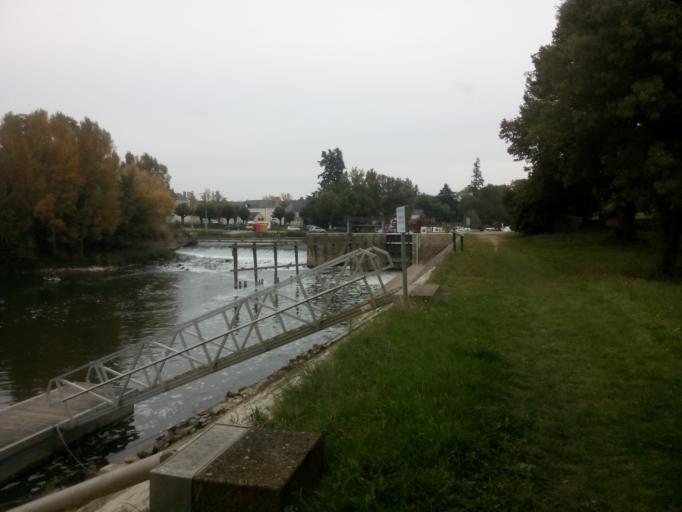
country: FR
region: Pays de la Loire
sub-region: Departement de Maine-et-Loire
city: Tierce
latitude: 47.6208
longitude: -0.5046
